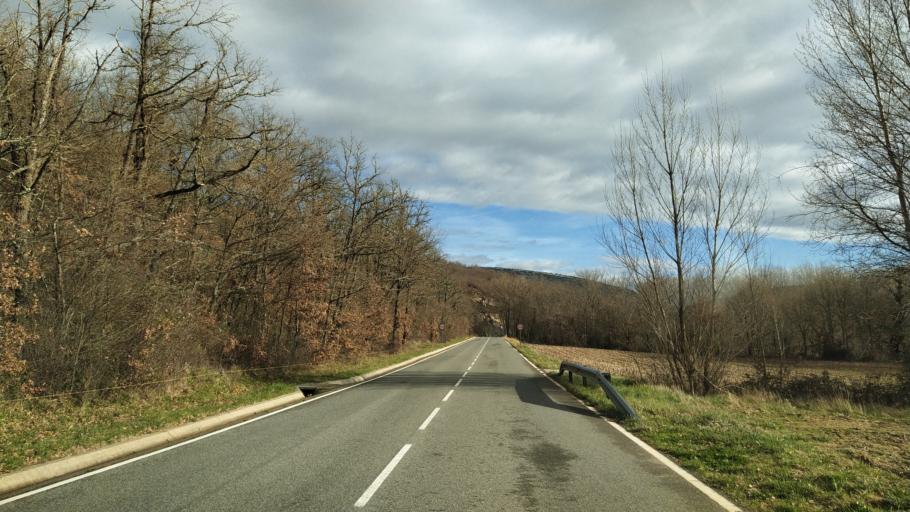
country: ES
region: Cantabria
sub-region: Provincia de Cantabria
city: San Martin de Elines
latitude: 42.8348
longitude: -3.8838
